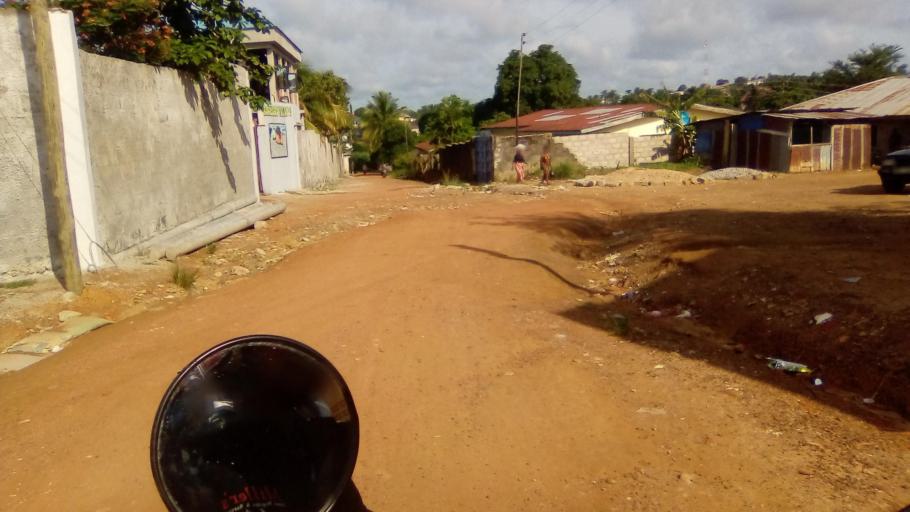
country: SL
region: Southern Province
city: Bo
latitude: 7.9554
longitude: -11.7615
